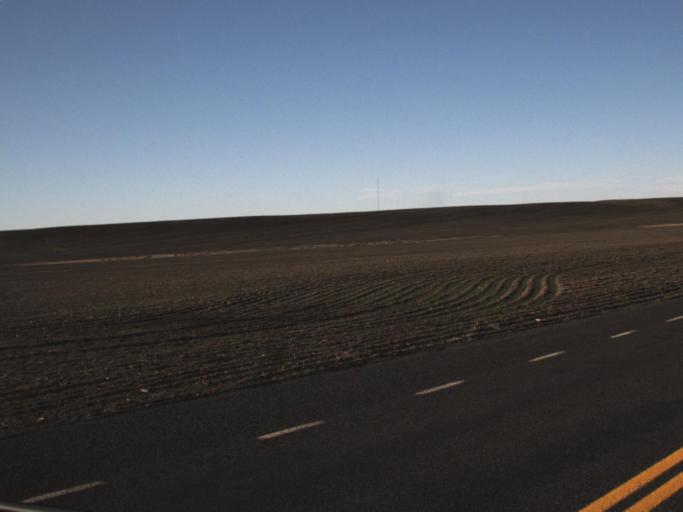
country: US
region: Washington
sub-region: Adams County
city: Ritzville
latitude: 46.8430
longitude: -118.3330
